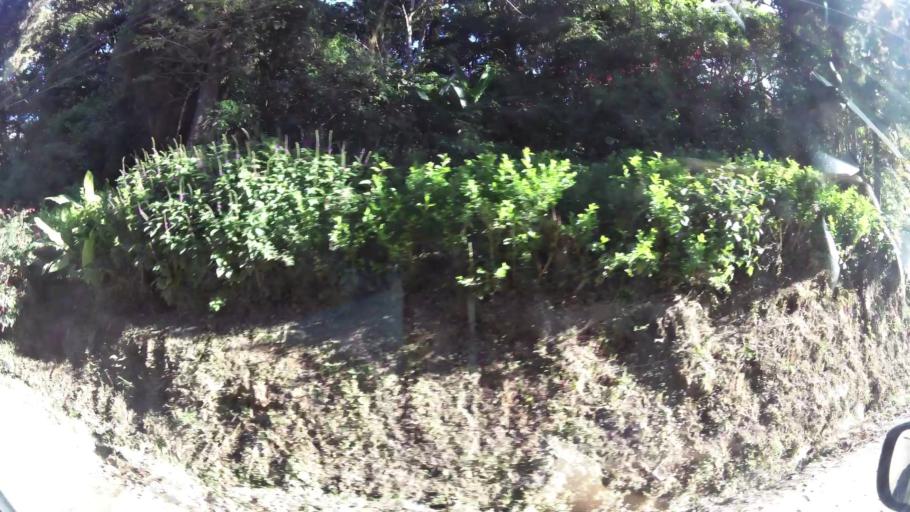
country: CR
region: Guanacaste
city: Juntas
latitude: 10.2998
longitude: -84.8053
